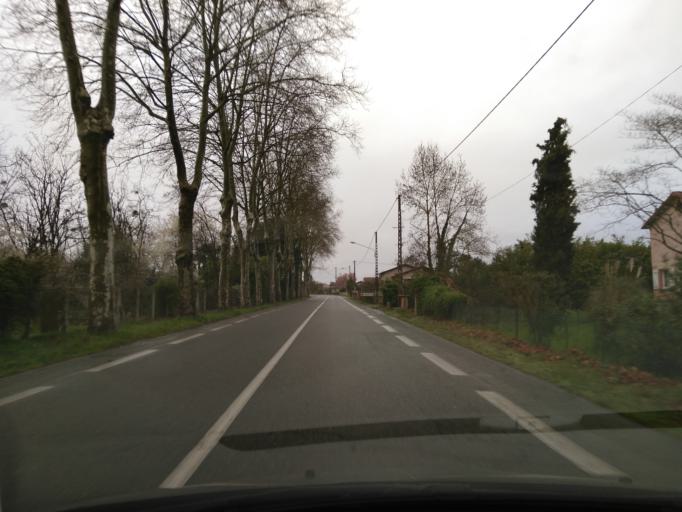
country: FR
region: Midi-Pyrenees
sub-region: Departement de la Haute-Garonne
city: Rieux-Volvestre
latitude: 43.2512
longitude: 1.2017
